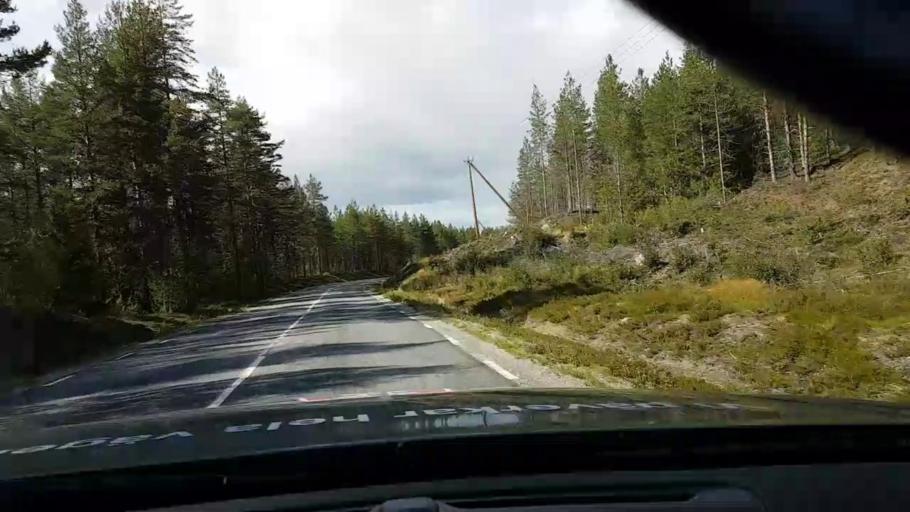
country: SE
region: Vaesterbotten
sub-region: Asele Kommun
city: Asele
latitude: 63.8502
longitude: 17.3971
